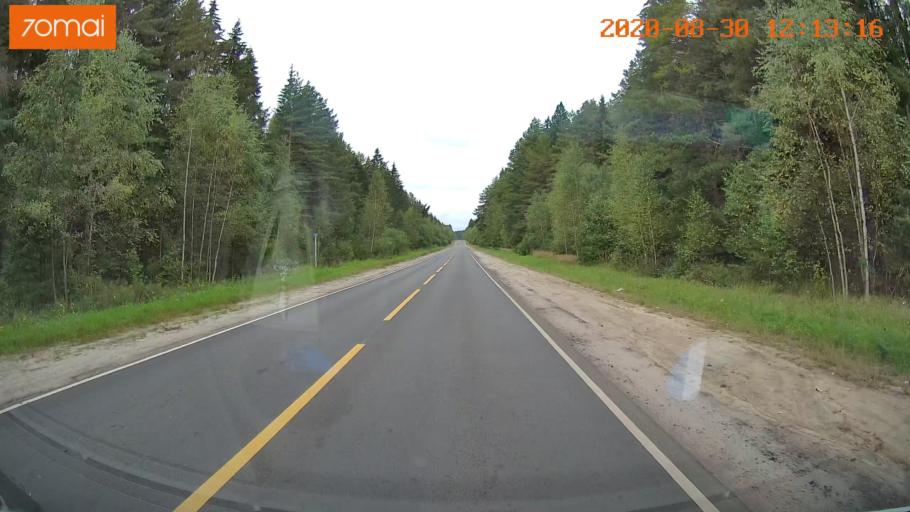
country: RU
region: Ivanovo
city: Yur'yevets
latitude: 57.3126
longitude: 43.0818
